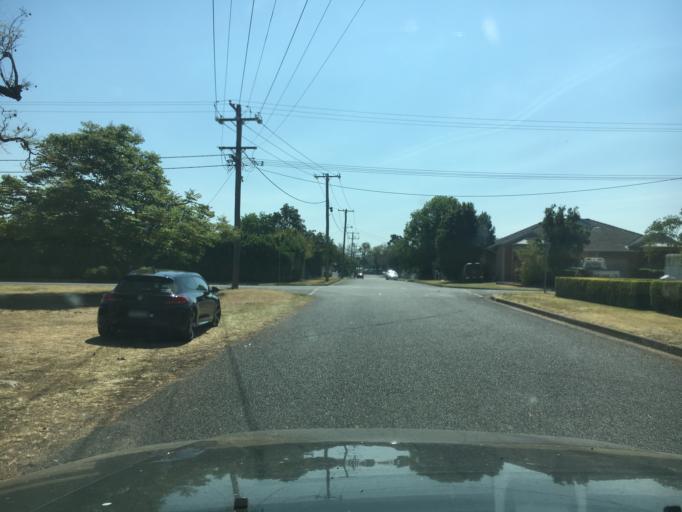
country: AU
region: New South Wales
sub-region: Singleton
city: Singleton
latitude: -32.5615
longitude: 151.1775
